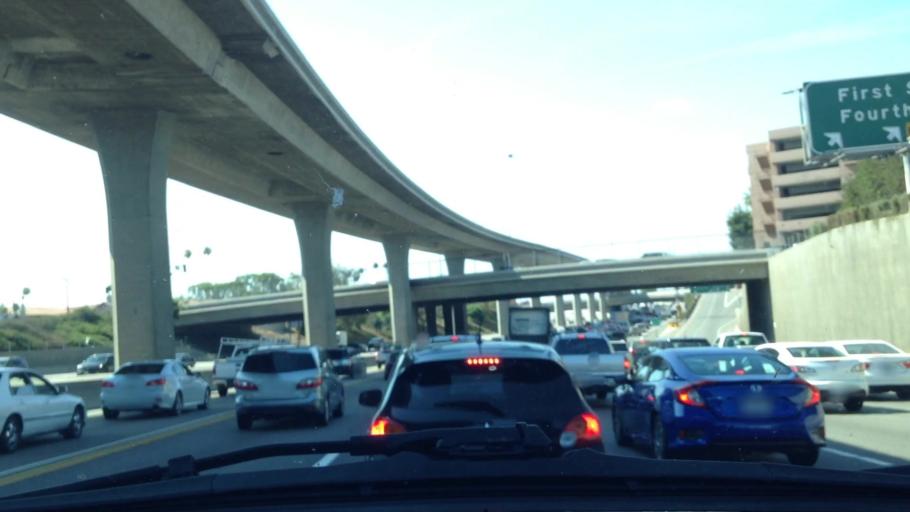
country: US
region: California
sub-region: Orange County
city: Tustin
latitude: 33.7446
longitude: -117.8416
